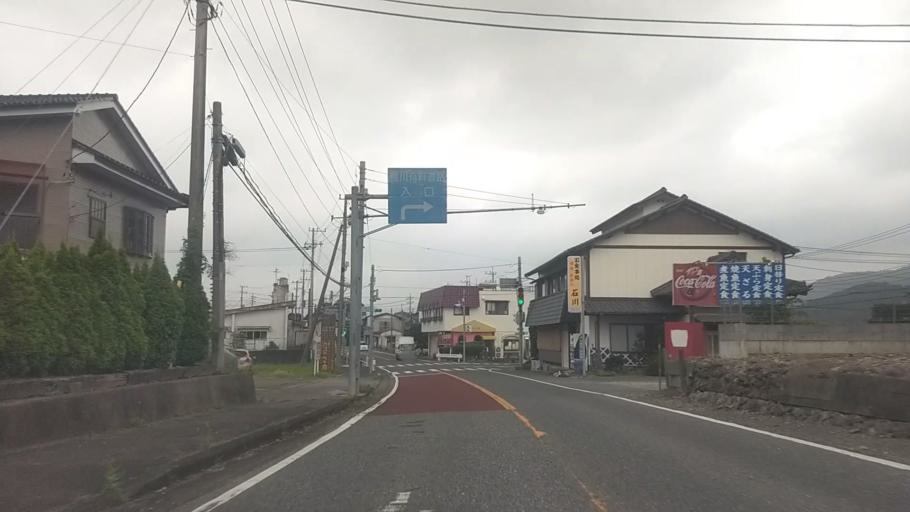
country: JP
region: Chiba
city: Kawaguchi
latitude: 35.1212
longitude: 140.0698
